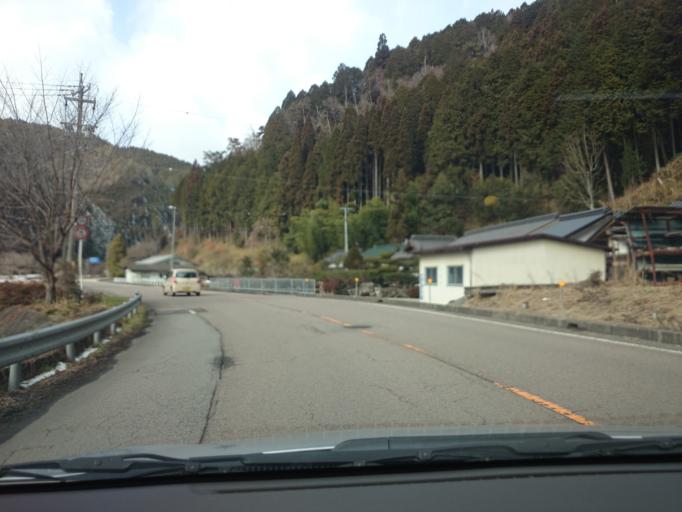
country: JP
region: Gifu
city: Gujo
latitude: 35.7394
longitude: 137.0548
